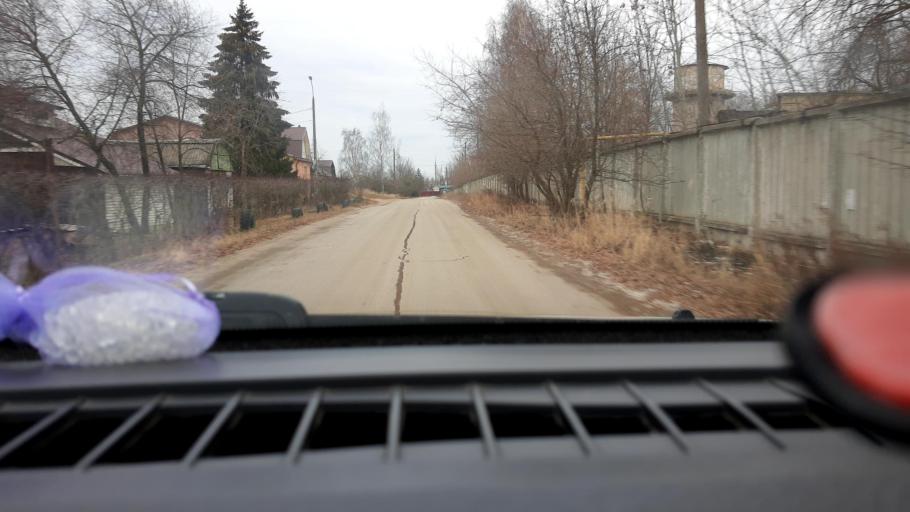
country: RU
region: Nizjnij Novgorod
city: Gorbatovka
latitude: 56.3825
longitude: 43.7788
